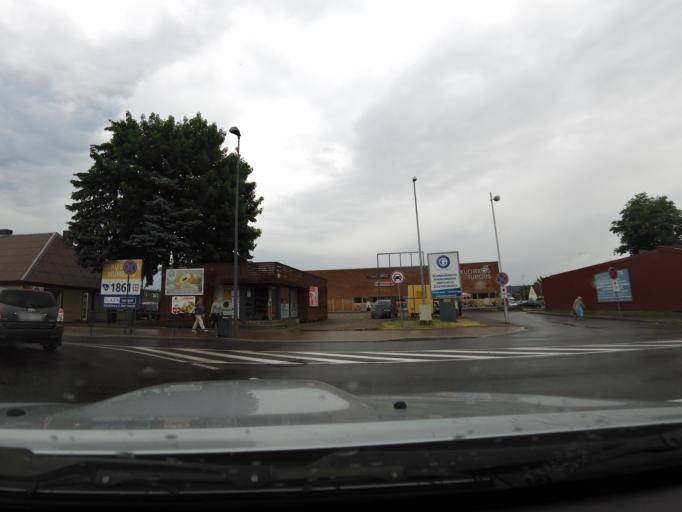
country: LT
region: Marijampoles apskritis
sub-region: Marijampole Municipality
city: Marijampole
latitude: 54.5547
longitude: 23.3539
